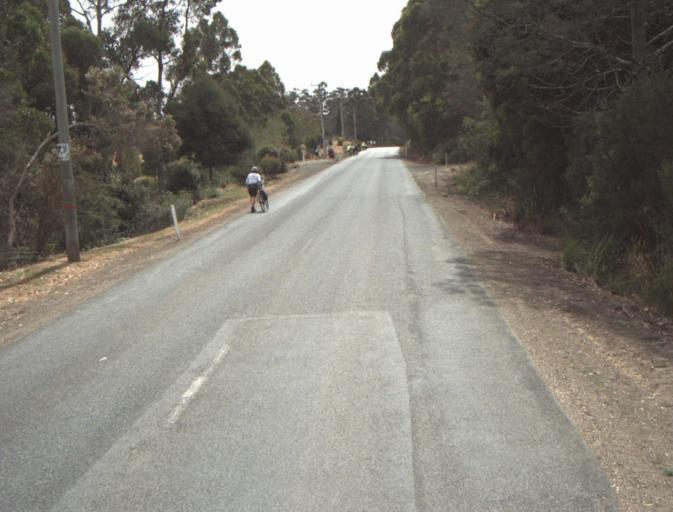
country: AU
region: Tasmania
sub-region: Launceston
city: Mayfield
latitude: -41.2176
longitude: 147.2086
